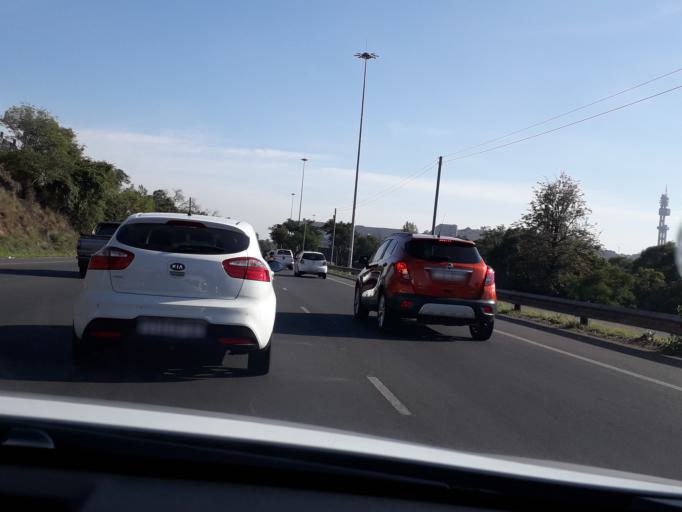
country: ZA
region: Gauteng
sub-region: City of Tshwane Metropolitan Municipality
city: Pretoria
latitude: -25.7790
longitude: 28.1933
